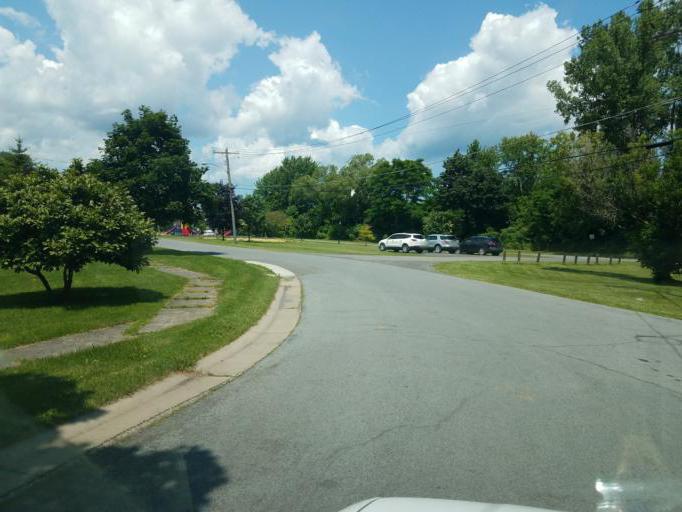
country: US
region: New York
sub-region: Wayne County
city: Clyde
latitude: 43.0792
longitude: -76.8687
